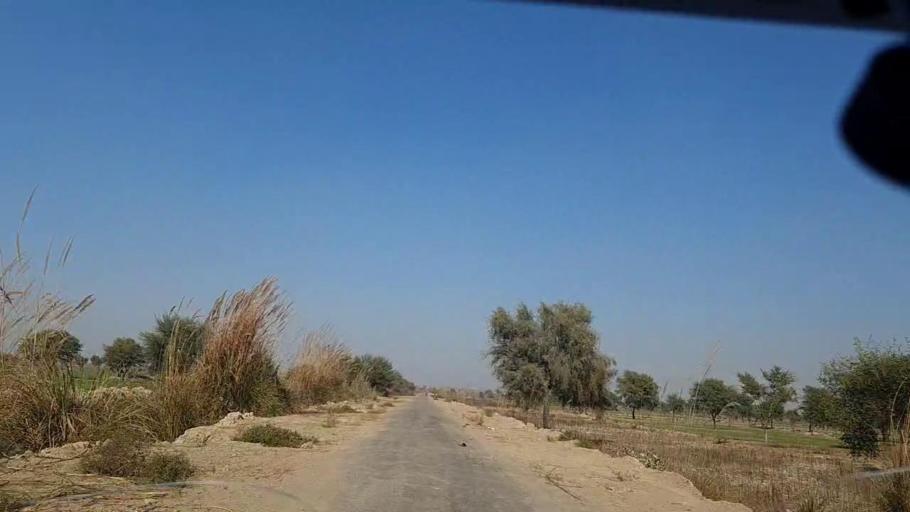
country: PK
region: Sindh
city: Khanpur
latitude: 27.5702
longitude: 69.3797
